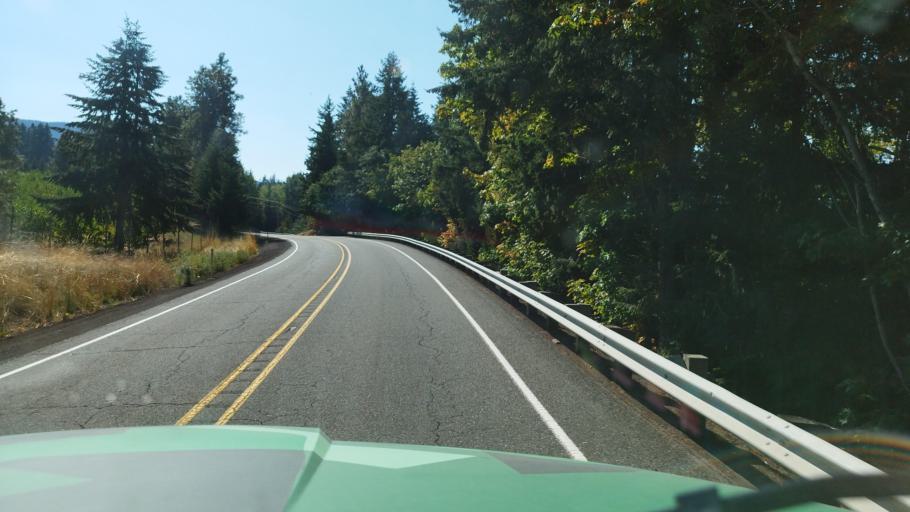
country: US
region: Oregon
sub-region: Hood River County
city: Odell
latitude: 45.5108
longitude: -121.5638
